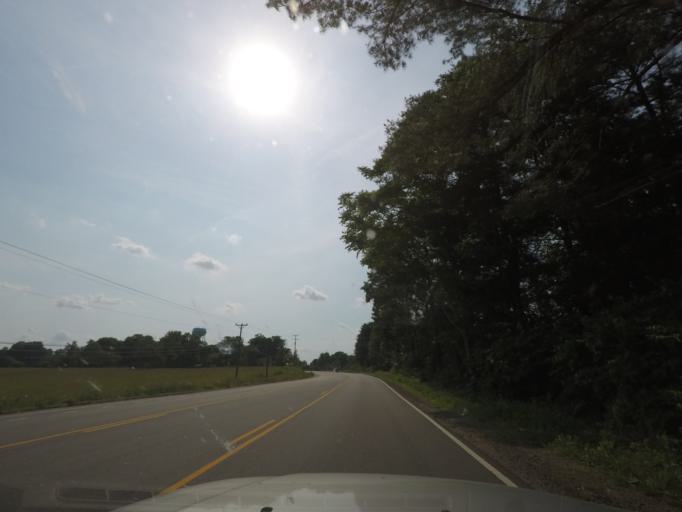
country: US
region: Virginia
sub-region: Buckingham County
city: Buckingham
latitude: 37.5457
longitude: -78.4665
